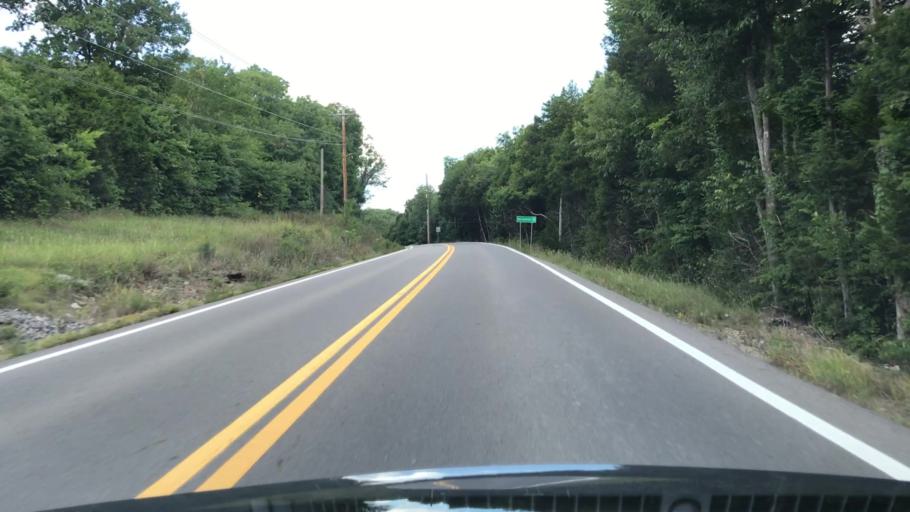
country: US
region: Tennessee
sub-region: Williamson County
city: Nolensville
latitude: 35.8514
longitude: -86.5997
